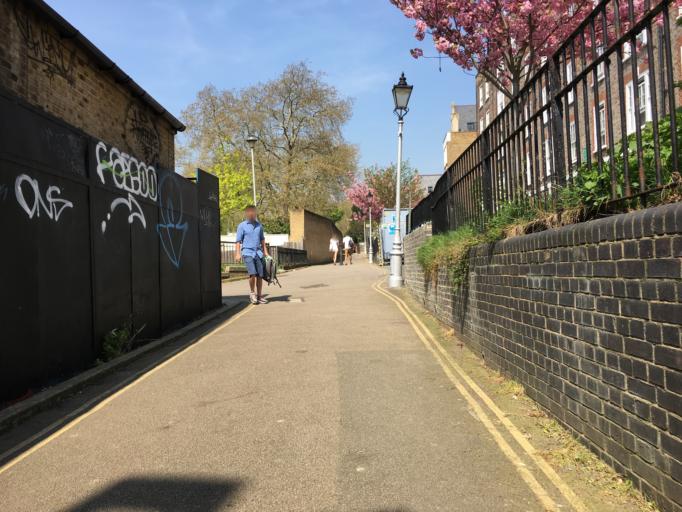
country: GB
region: England
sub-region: Greater London
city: Camden Town
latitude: 51.5562
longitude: -0.1453
